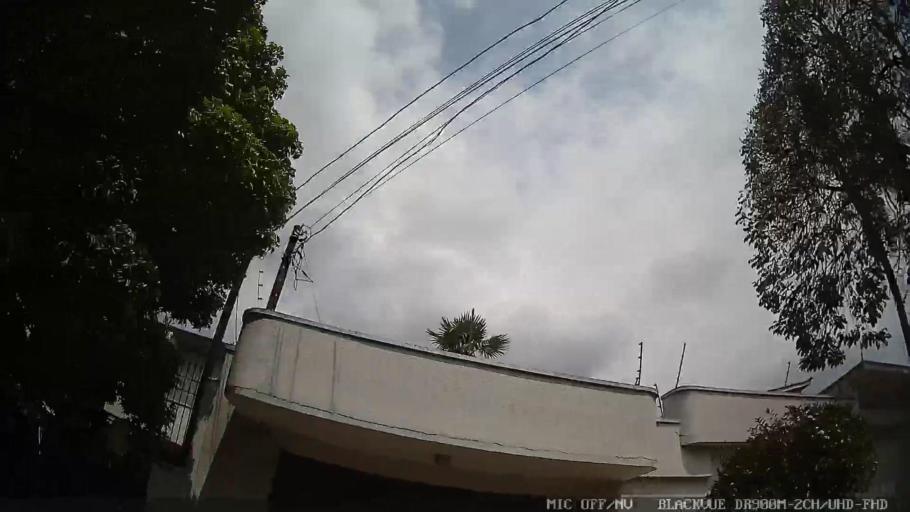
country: BR
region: Sao Paulo
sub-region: Diadema
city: Diadema
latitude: -23.6354
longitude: -46.6710
